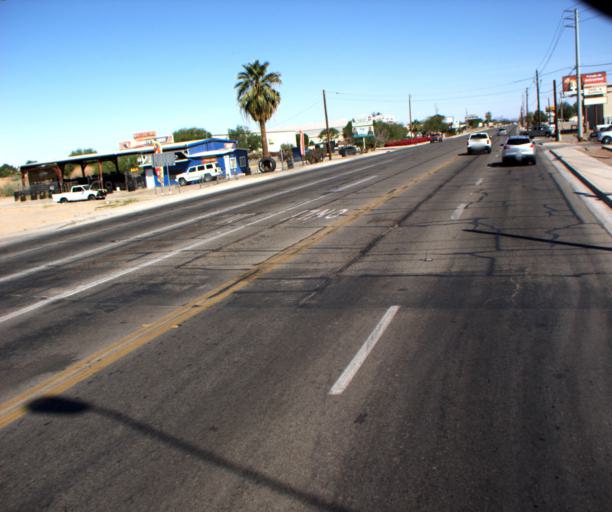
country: US
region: Arizona
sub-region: Yuma County
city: Yuma
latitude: 32.6697
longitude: -114.6500
